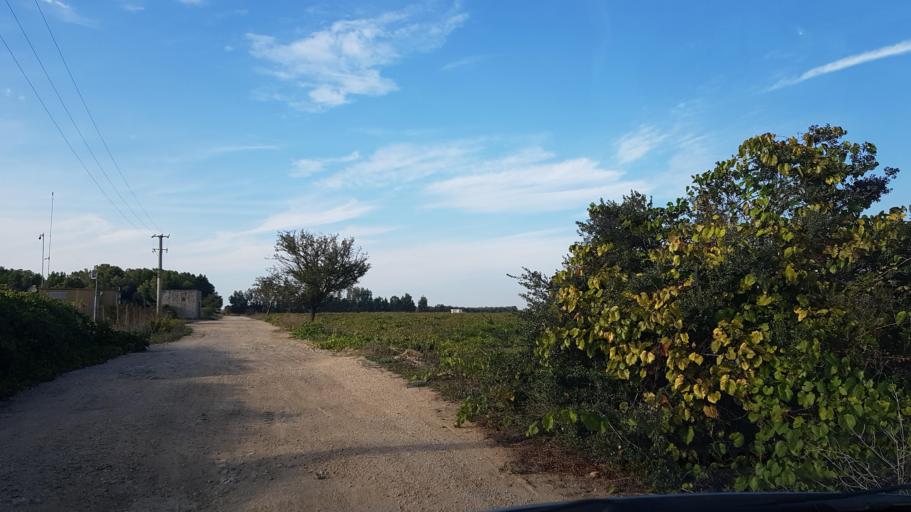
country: IT
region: Apulia
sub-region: Provincia di Brindisi
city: San Pancrazio Salentino
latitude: 40.4893
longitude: 17.8563
